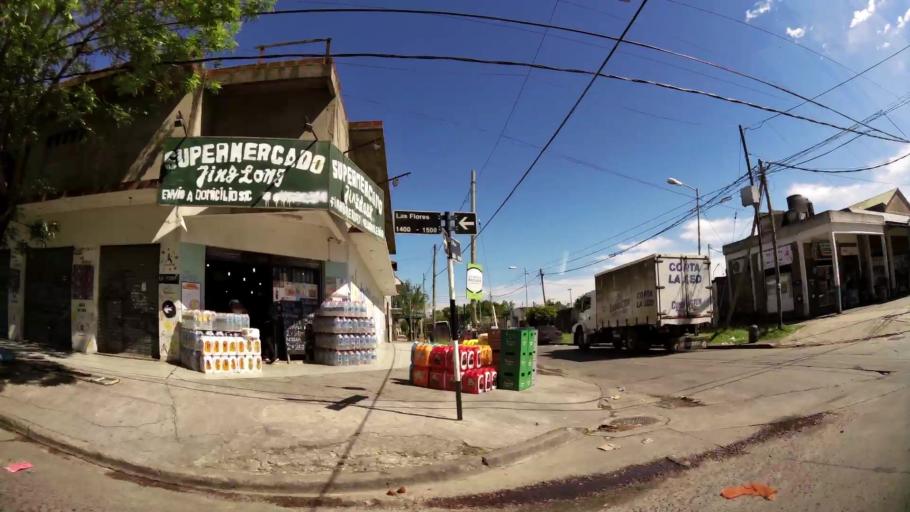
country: AR
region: Buenos Aires
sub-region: Partido de Quilmes
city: Quilmes
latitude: -34.6917
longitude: -58.3037
